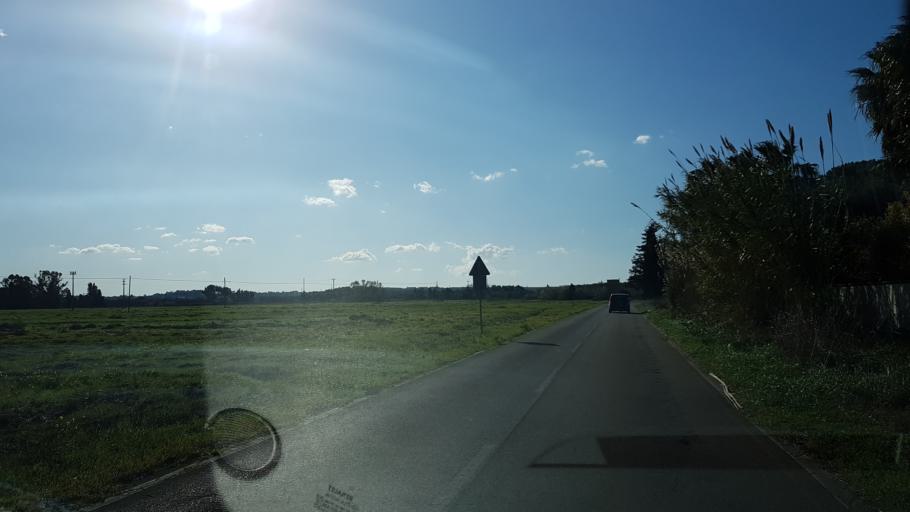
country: IT
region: Apulia
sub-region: Provincia di Lecce
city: Gallipoli
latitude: 40.0882
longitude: 18.0151
